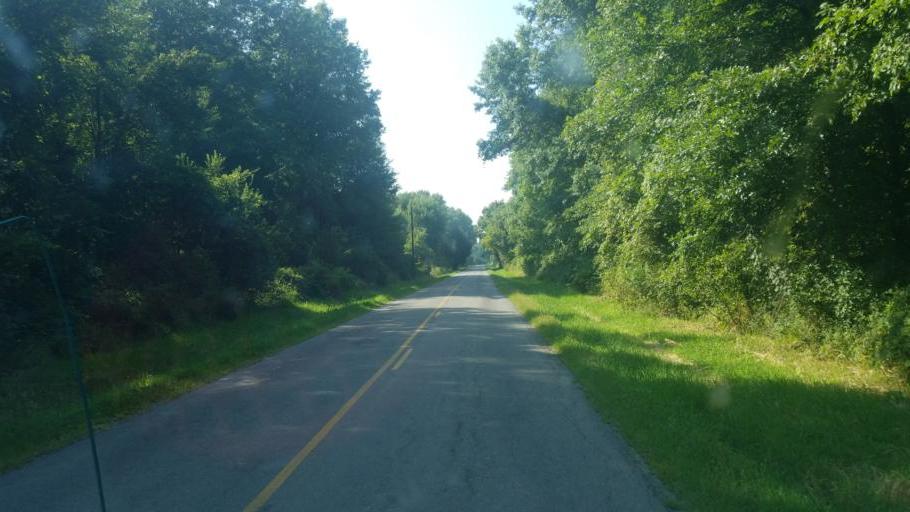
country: US
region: Ohio
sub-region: Medina County
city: Lodi
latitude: 41.0140
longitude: -82.0353
